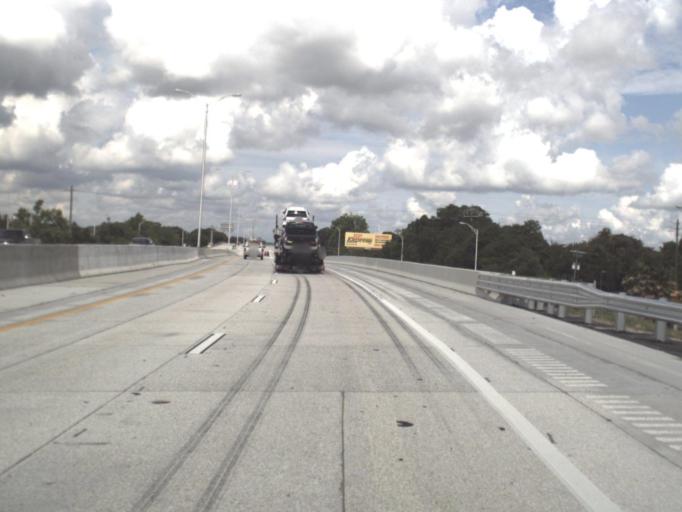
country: US
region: Florida
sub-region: Duval County
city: Jacksonville
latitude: 30.3563
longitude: -81.6399
